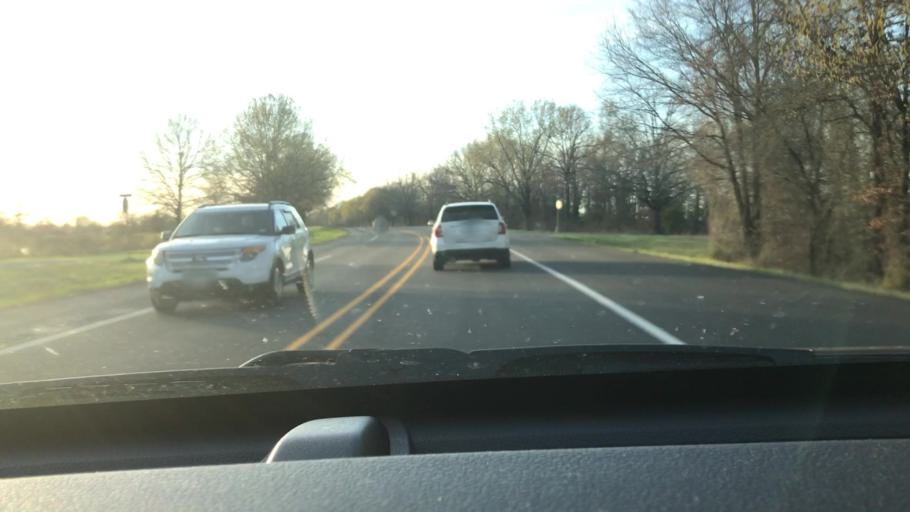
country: US
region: Texas
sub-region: Red River County
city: Clarksville
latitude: 33.5890
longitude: -94.9425
